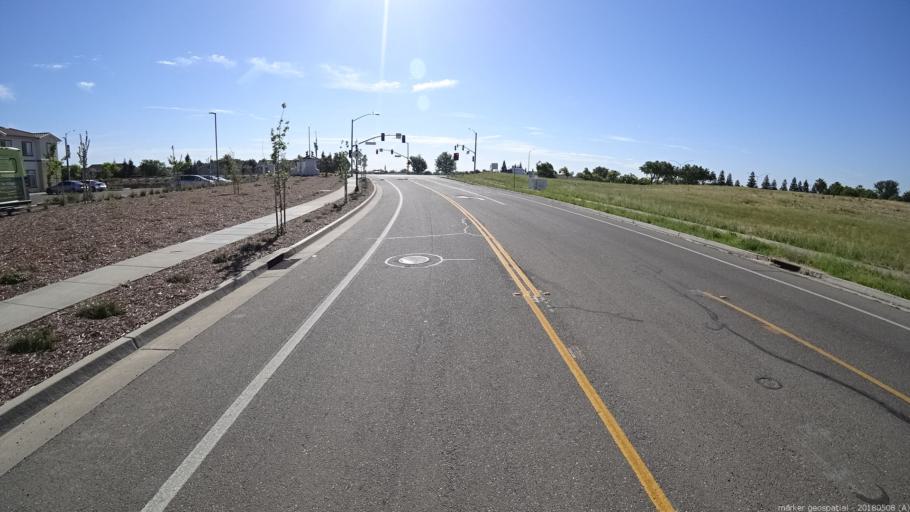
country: US
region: California
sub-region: Sacramento County
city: Elverta
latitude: 38.6821
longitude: -121.5092
